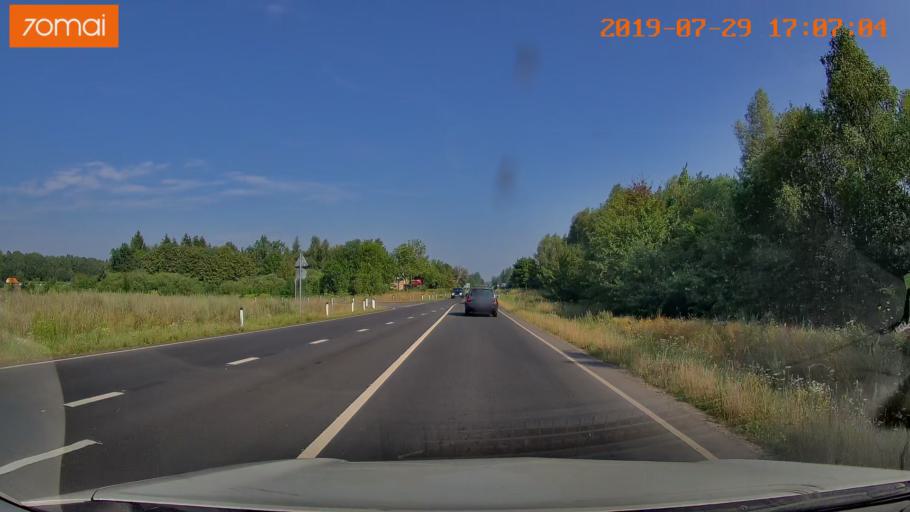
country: RU
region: Kaliningrad
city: Vzmorye
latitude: 54.8184
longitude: 20.3167
